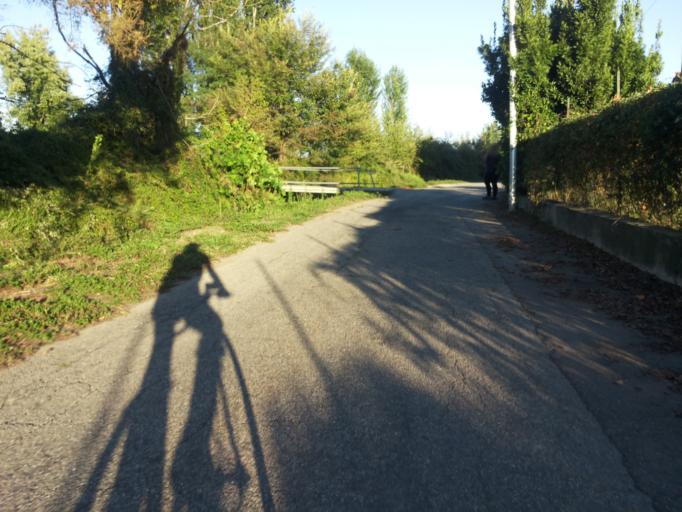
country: IT
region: Piedmont
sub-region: Provincia di Vercelli
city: Pezzana
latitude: 45.2601
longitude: 8.4944
